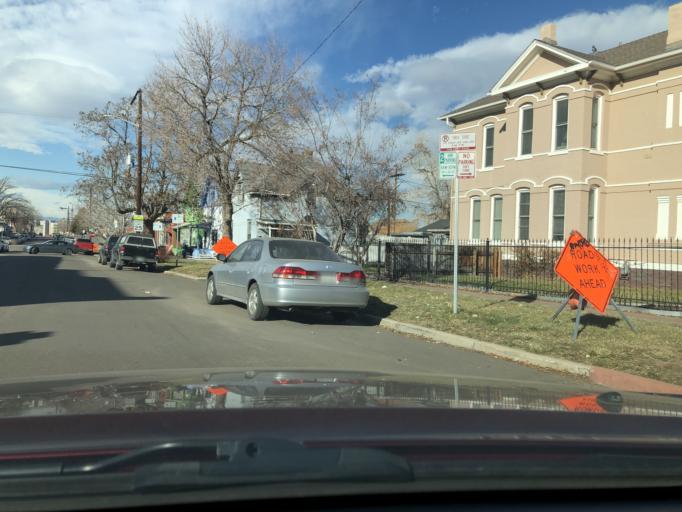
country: US
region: Colorado
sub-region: Denver County
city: Denver
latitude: 39.7566
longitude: -104.9828
